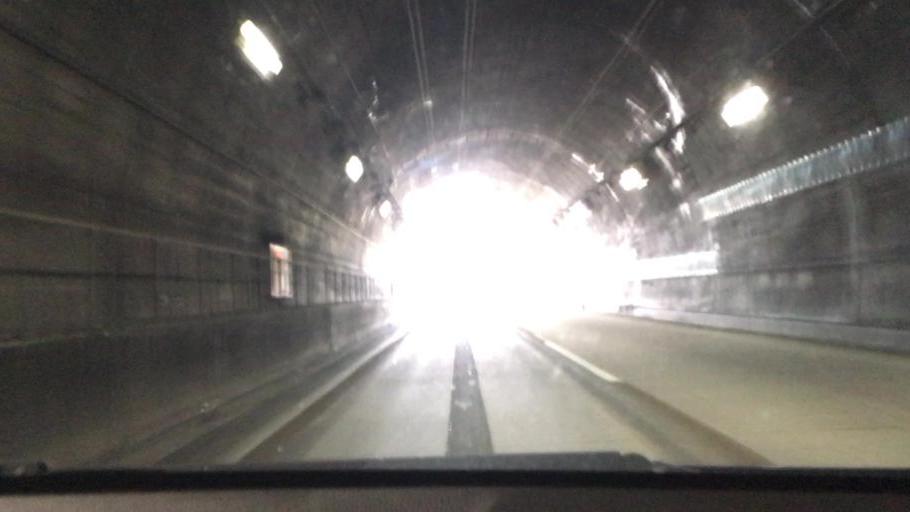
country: JP
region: Yamaguchi
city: Hofu
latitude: 34.0689
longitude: 131.6611
